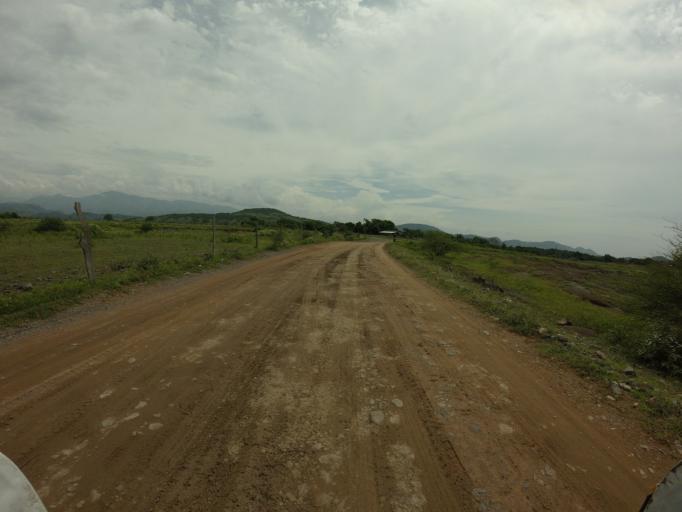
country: CO
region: Tolima
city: Natagaima
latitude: 3.4640
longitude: -75.1412
